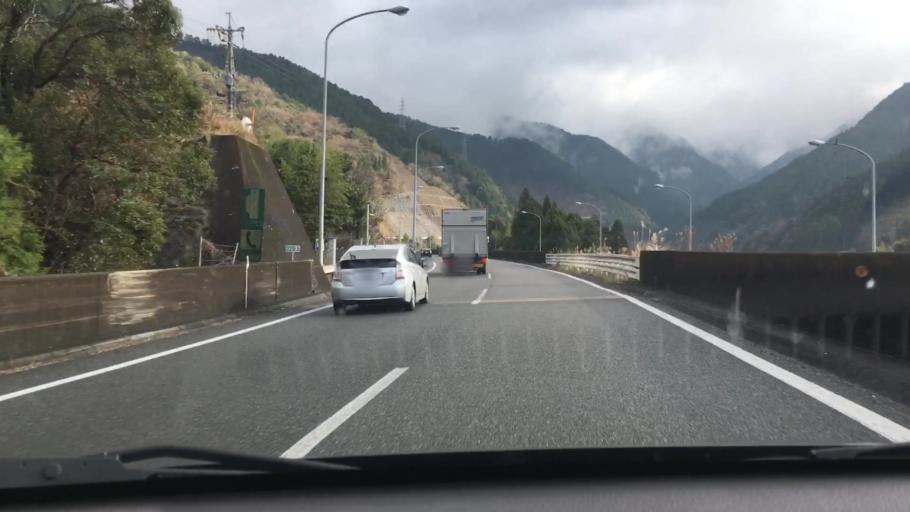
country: JP
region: Kumamoto
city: Yatsushiro
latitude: 32.4018
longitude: 130.6986
